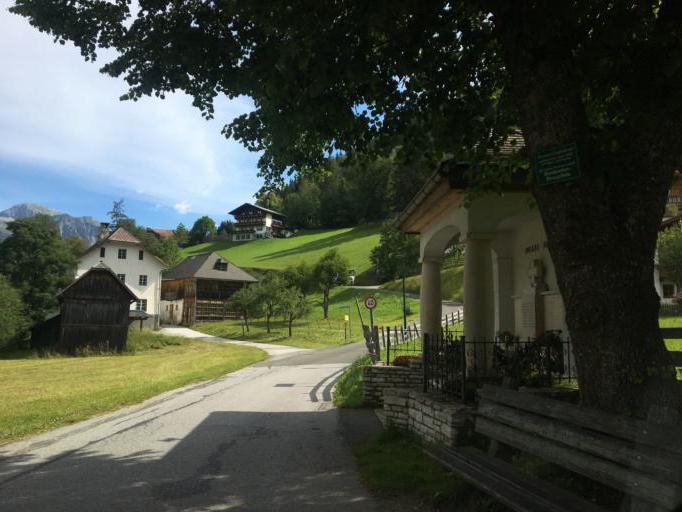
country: AT
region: Styria
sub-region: Politischer Bezirk Liezen
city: Schladming
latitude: 47.3732
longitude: 13.6771
